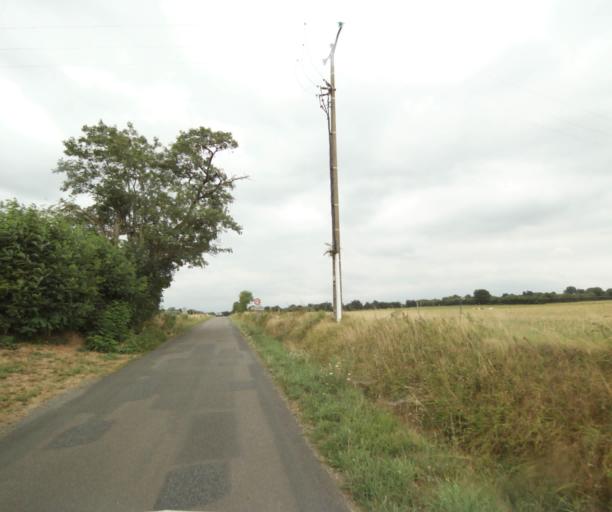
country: FR
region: Pays de la Loire
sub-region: Departement de la Sarthe
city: Solesmes
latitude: 47.8503
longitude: -0.2873
